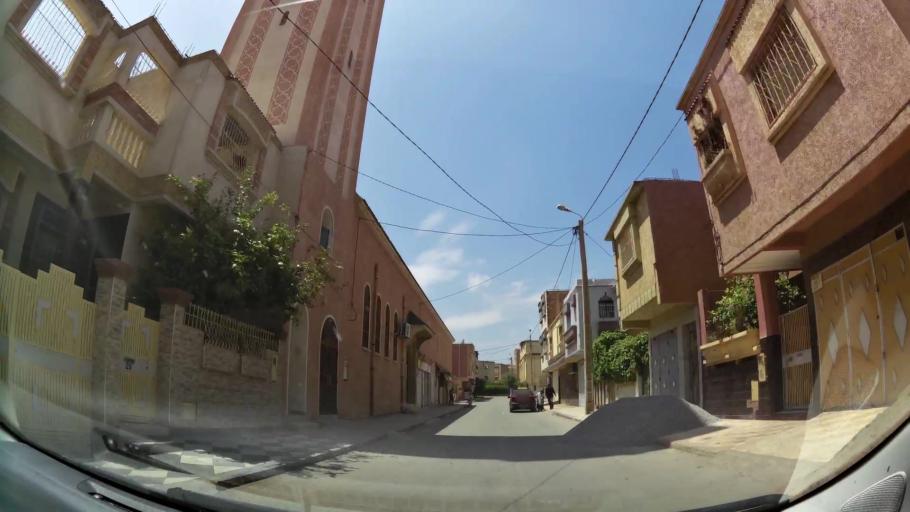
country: MA
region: Oriental
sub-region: Oujda-Angad
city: Oujda
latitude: 34.6905
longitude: -1.8890
